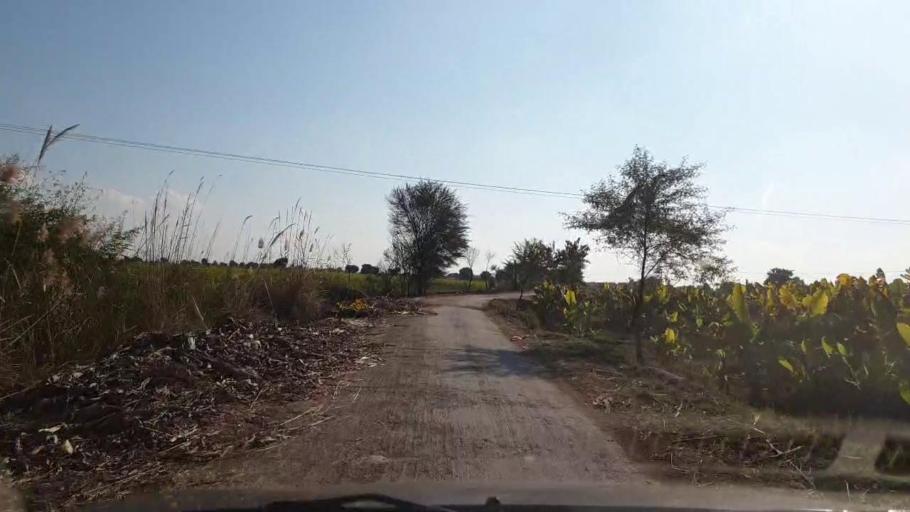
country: PK
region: Sindh
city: Sinjhoro
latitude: 25.9930
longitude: 68.7277
